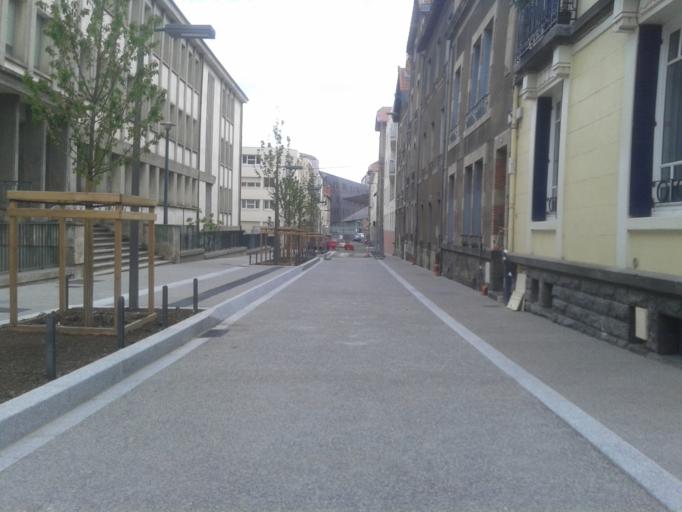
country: FR
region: Auvergne
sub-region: Departement du Puy-de-Dome
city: Clermont-Ferrand
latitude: 45.7703
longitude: 3.0873
